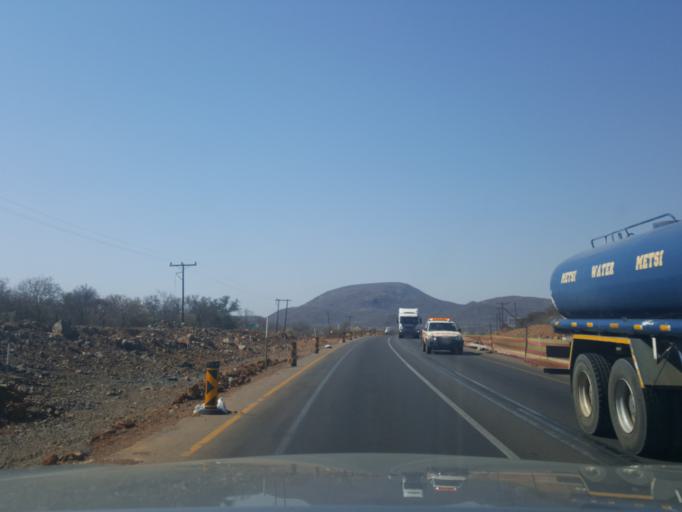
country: BW
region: Kweneng
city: Gabane
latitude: -24.7475
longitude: 25.8295
